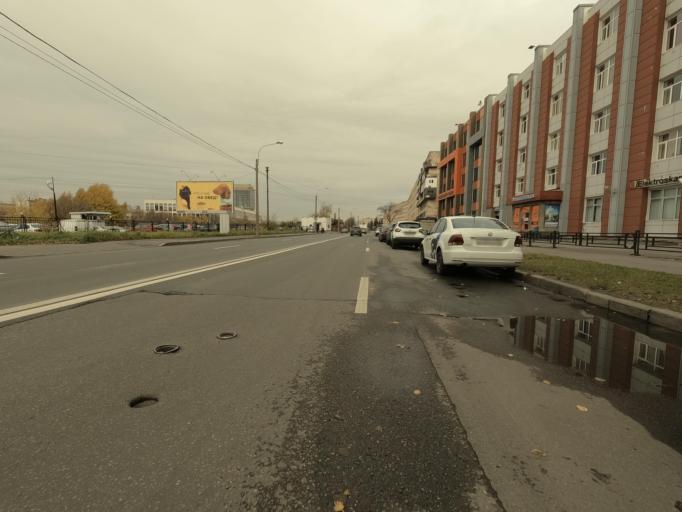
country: RU
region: St.-Petersburg
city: Centralniy
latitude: 59.9390
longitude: 30.4149
